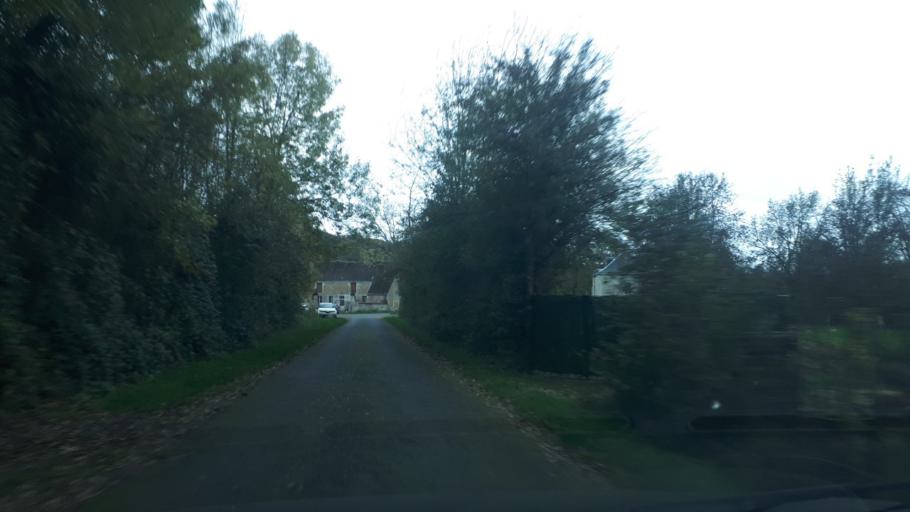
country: FR
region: Centre
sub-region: Departement du Loir-et-Cher
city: Lunay
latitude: 47.7714
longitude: 0.9534
